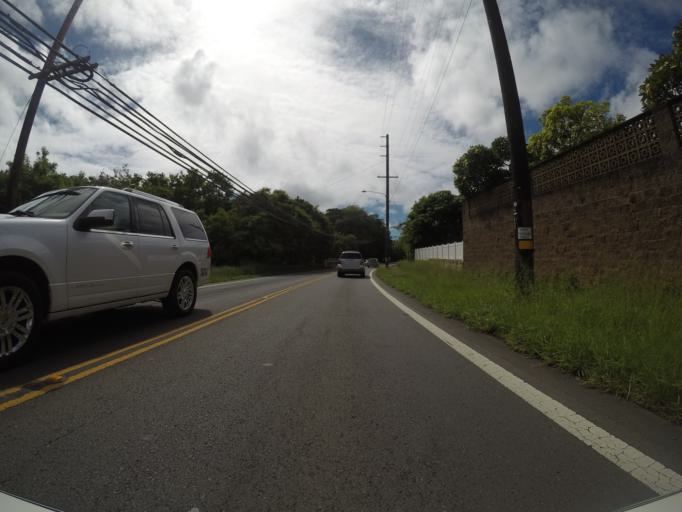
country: US
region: Hawaii
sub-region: Honolulu County
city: Waimanalo
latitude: 21.3464
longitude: -157.7120
